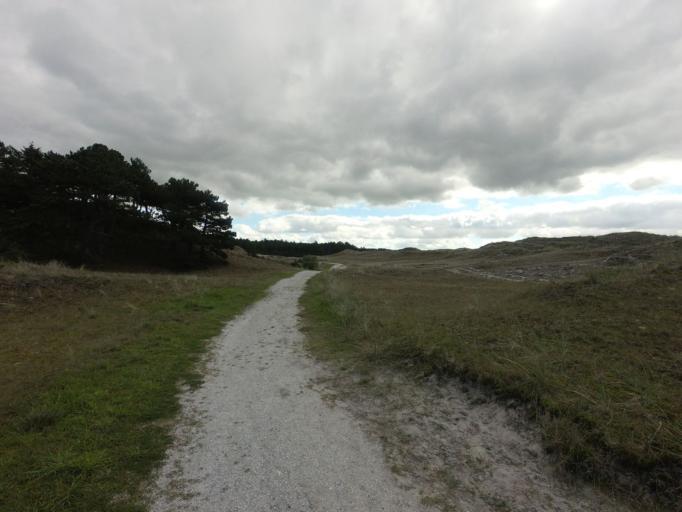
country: NL
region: North Holland
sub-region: Gemeente Bergen
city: Egmond aan Zee
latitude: 52.7116
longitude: 4.6618
